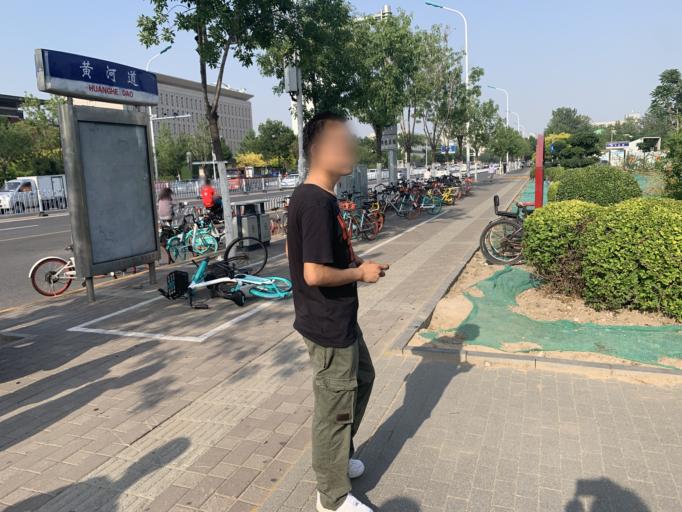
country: CN
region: Tianjin Shi
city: Xiangyanglu
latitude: 39.1364
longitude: 117.1283
